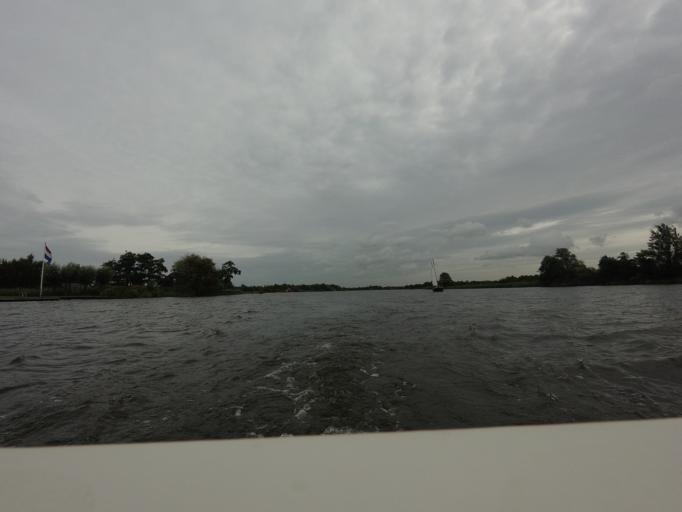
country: NL
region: Friesland
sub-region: Gemeente Boarnsterhim
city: Warten
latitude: 53.1224
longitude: 5.9138
